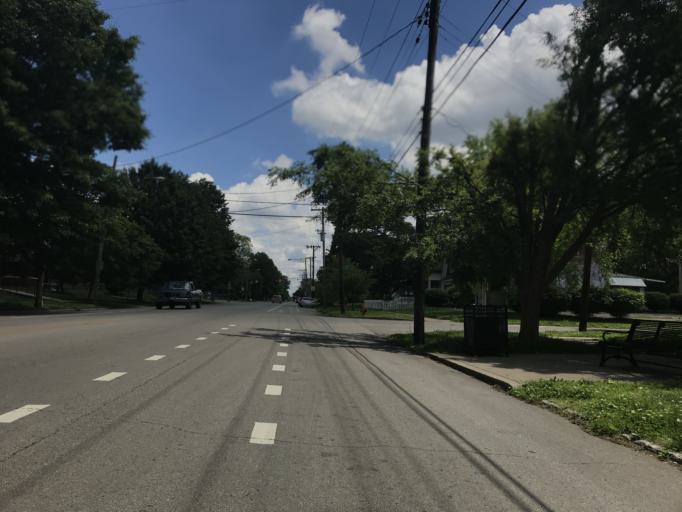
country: US
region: Indiana
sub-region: Floyd County
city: New Albany
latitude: 38.2501
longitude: -85.8167
